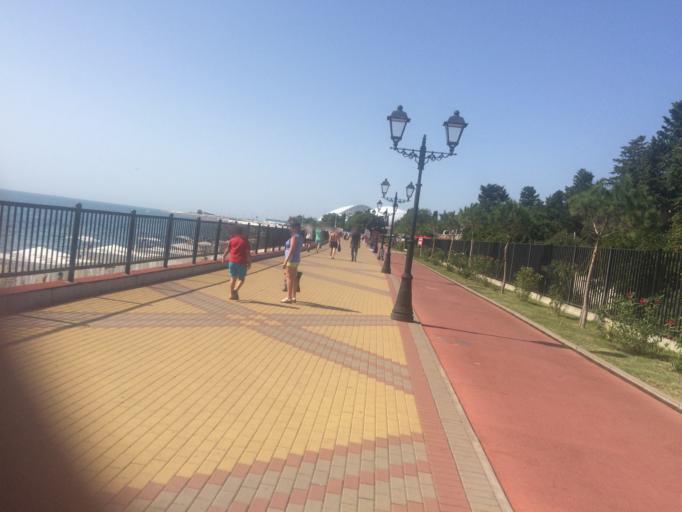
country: RU
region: Krasnodarskiy
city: Adler
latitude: 43.3964
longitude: 39.9699
